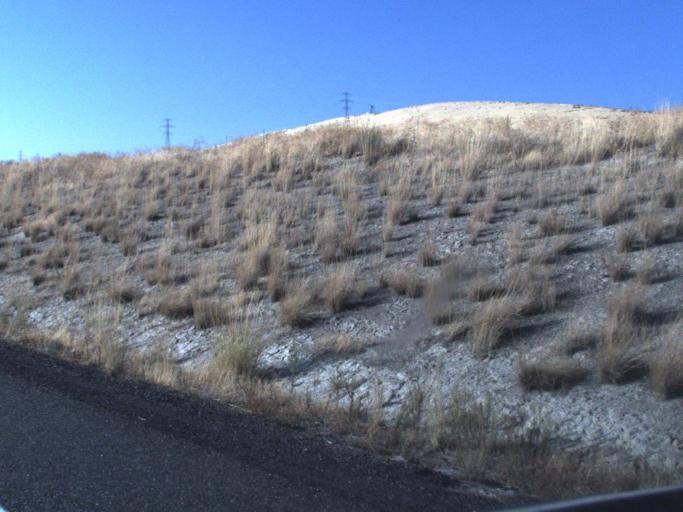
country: US
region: Washington
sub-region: Benton County
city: Highland
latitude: 46.1537
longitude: -119.1465
